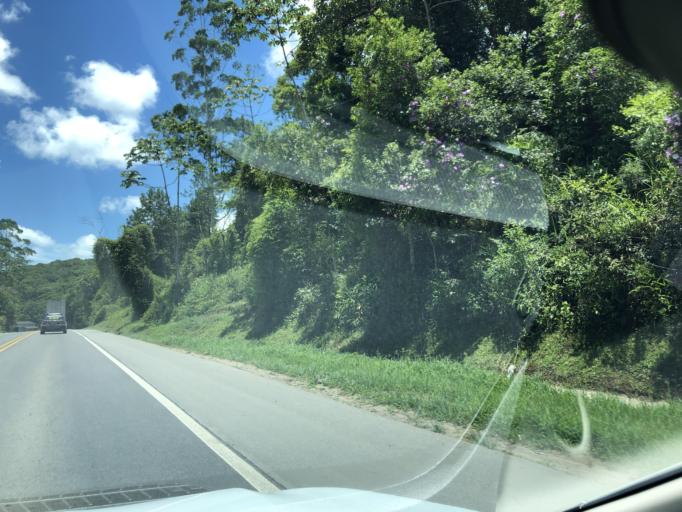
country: BR
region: Santa Catarina
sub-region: Joinville
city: Joinville
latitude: -26.4323
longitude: -48.8013
